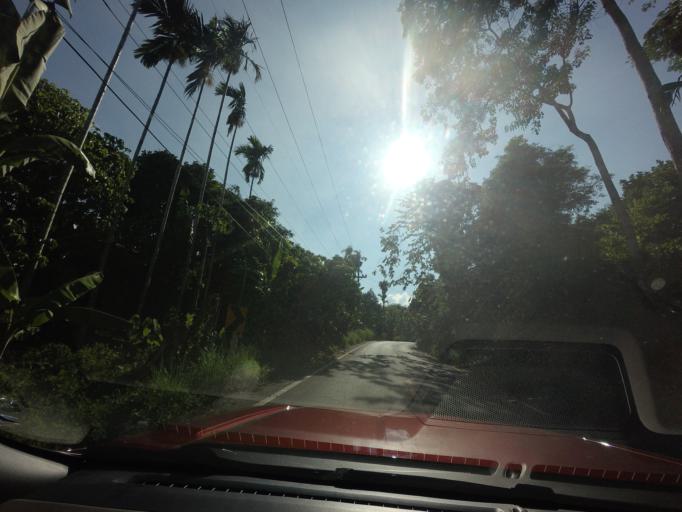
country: TH
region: Yala
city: Than To
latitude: 6.0710
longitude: 101.3480
